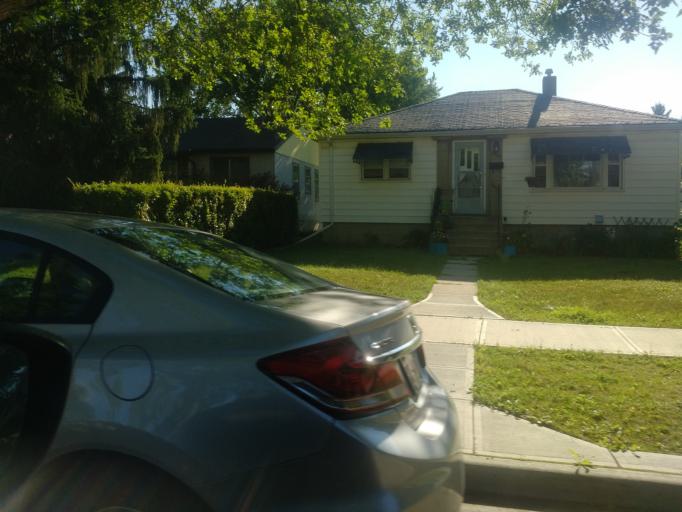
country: CA
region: Alberta
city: Edmonton
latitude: 53.5016
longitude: -113.5217
